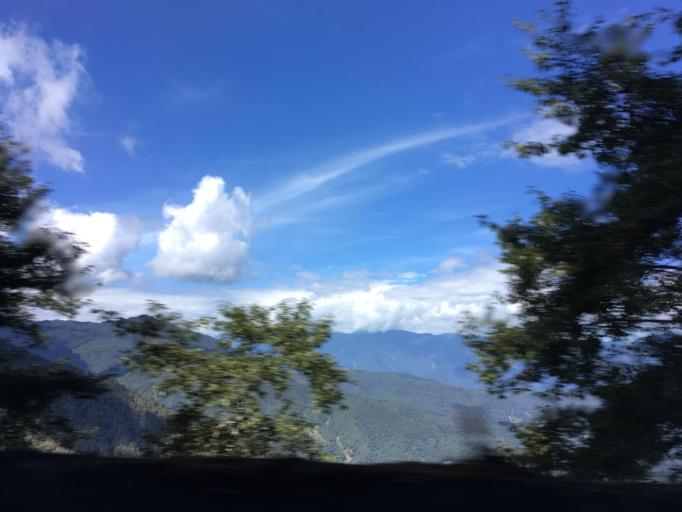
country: TW
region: Taiwan
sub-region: Yilan
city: Yilan
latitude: 24.5078
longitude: 121.5249
